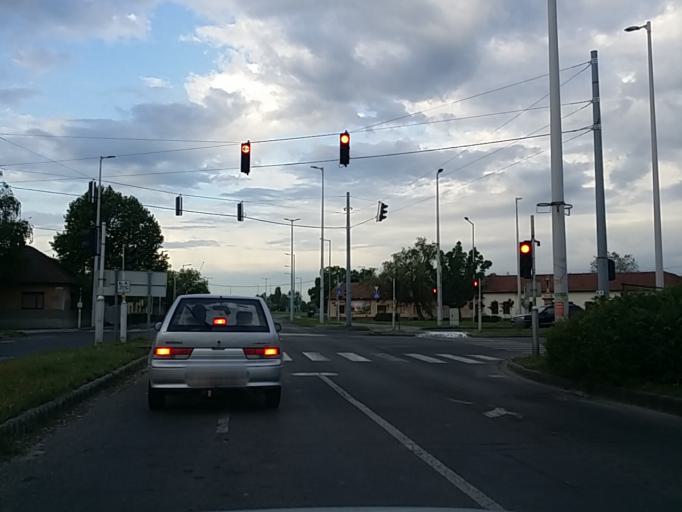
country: HU
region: Bacs-Kiskun
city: Kecskemet
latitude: 46.9024
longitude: 19.7049
